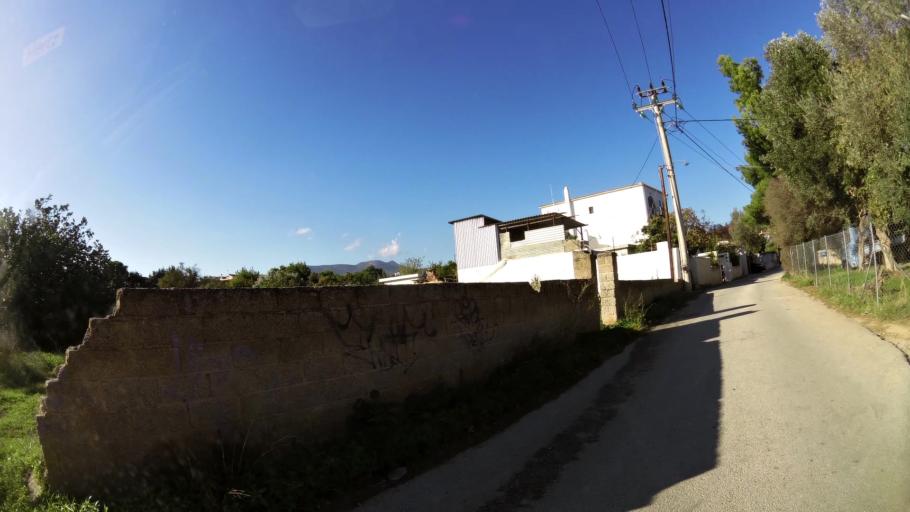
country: GR
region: Attica
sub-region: Nomarchia Anatolikis Attikis
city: Rafina
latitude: 38.0191
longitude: 23.9850
